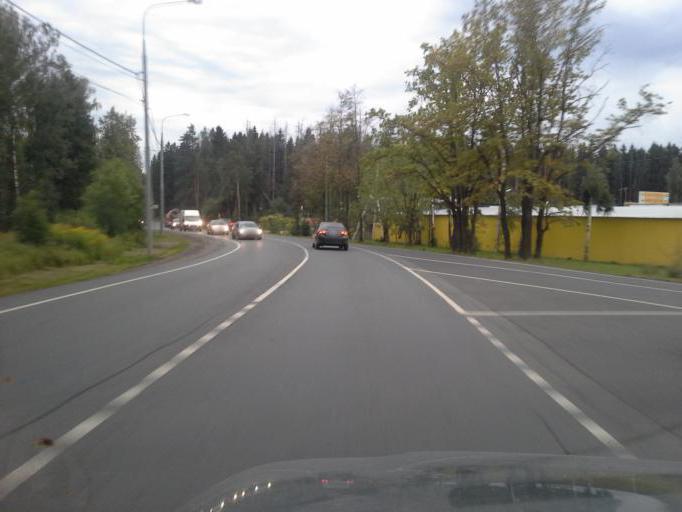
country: RU
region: Moskovskaya
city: Zhavoronki
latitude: 55.6622
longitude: 37.0934
